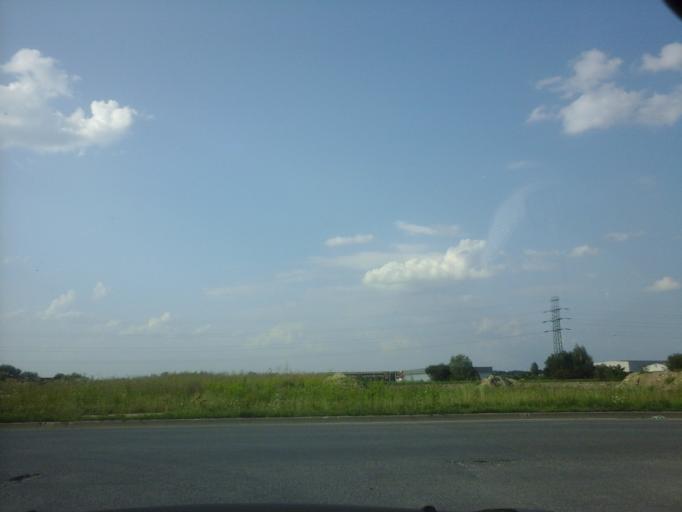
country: PL
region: Lesser Poland Voivodeship
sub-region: Powiat wielicki
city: Czarnochowice
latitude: 50.0328
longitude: 20.0521
